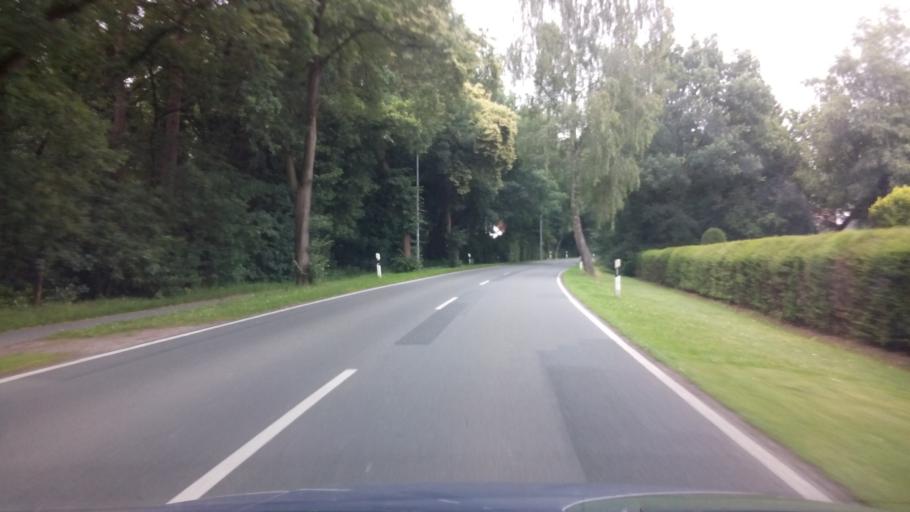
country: DE
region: Lower Saxony
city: Worpswede
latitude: 53.2098
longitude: 8.9307
